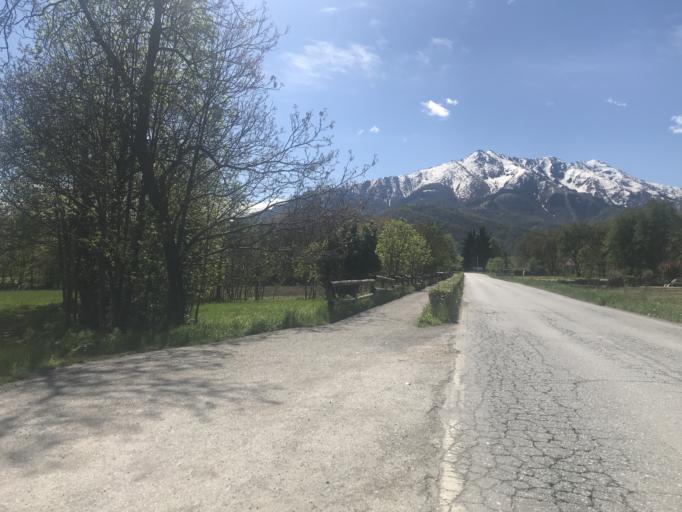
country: IT
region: Piedmont
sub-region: Provincia di Cuneo
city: Boves
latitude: 44.3239
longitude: 7.5621
